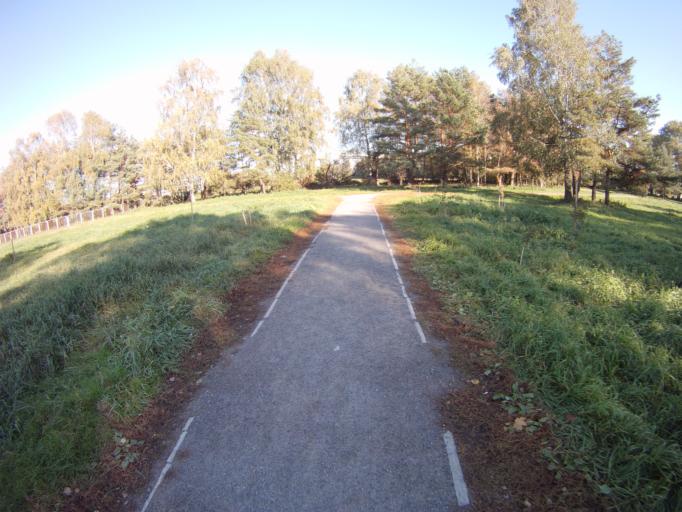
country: BY
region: Minsk
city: Minsk
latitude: 53.9337
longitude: 27.5718
